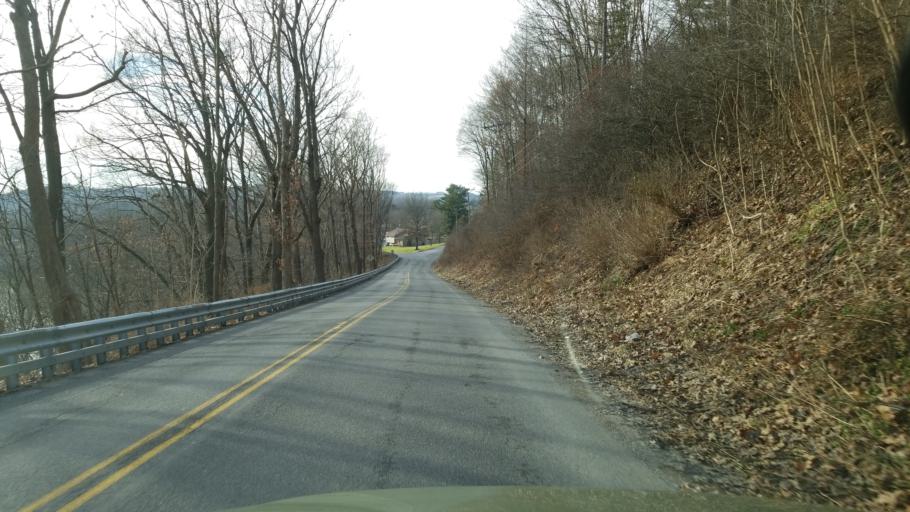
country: US
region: Pennsylvania
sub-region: Clearfield County
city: Clearfield
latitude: 41.0157
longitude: -78.4478
